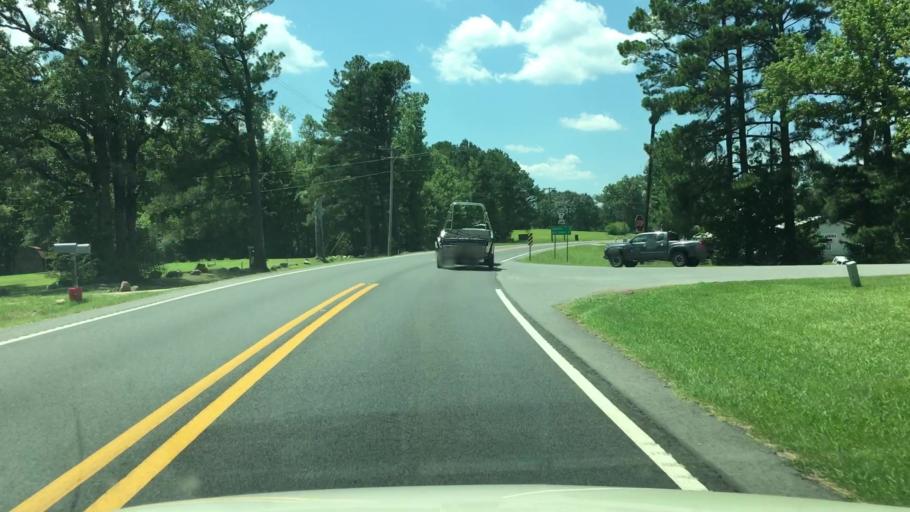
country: US
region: Arkansas
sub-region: Garland County
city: Lake Hamilton
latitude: 34.2651
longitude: -93.1361
